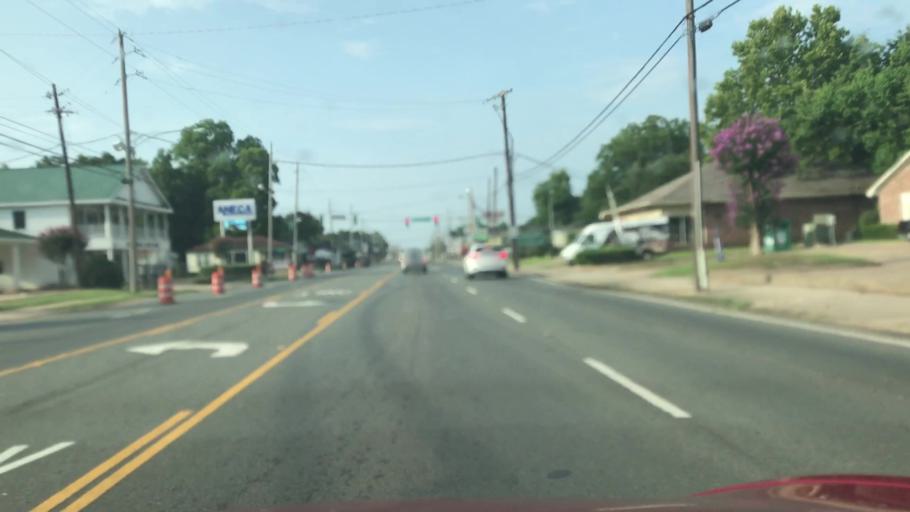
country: US
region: Louisiana
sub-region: Bossier Parish
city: Bossier City
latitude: 32.4611
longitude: -93.7222
